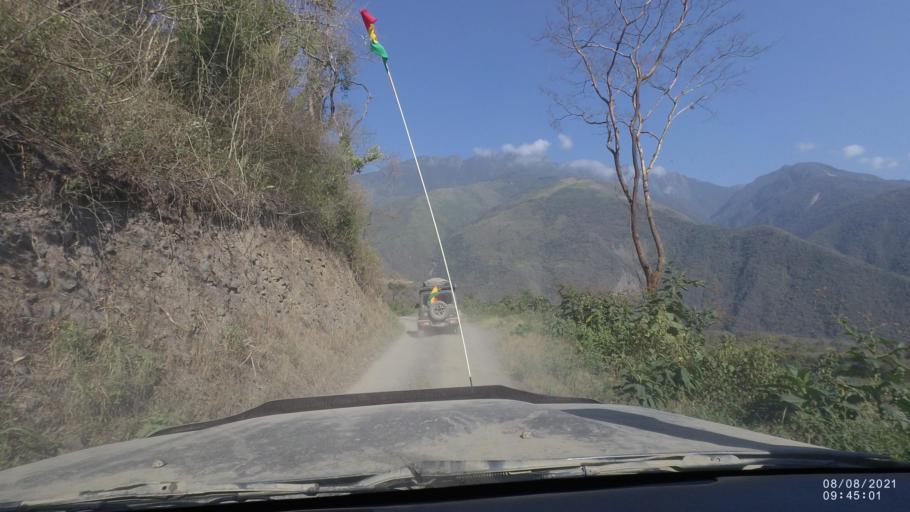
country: BO
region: La Paz
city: Quime
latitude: -16.6028
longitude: -66.7250
